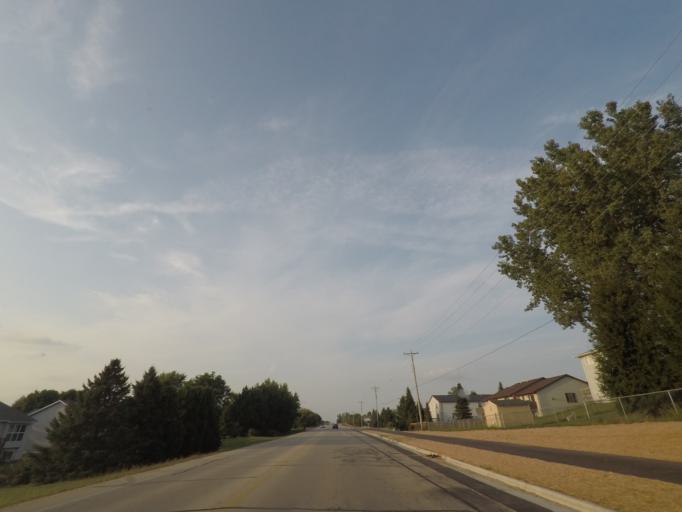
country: US
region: Wisconsin
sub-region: Dane County
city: Cottage Grove
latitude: 43.0924
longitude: -89.1996
